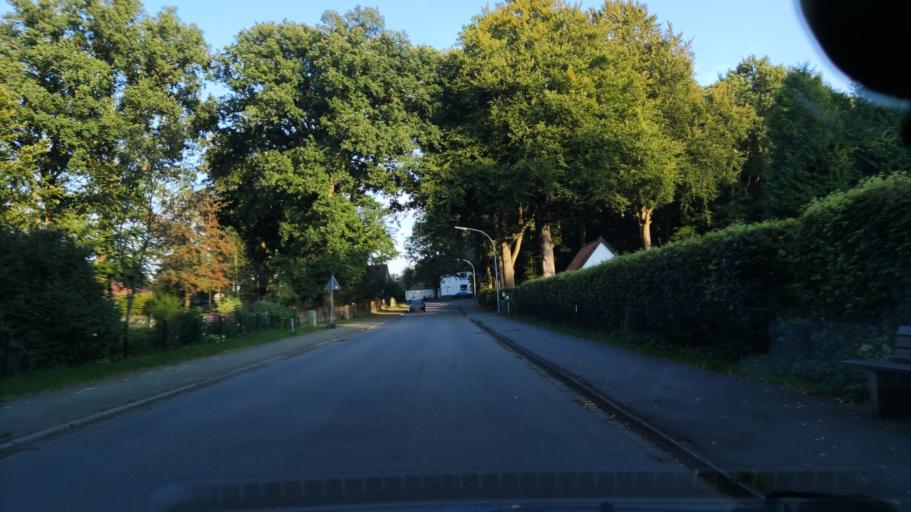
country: DE
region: Lower Saxony
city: Fassberg
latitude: 52.9623
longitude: 10.1823
